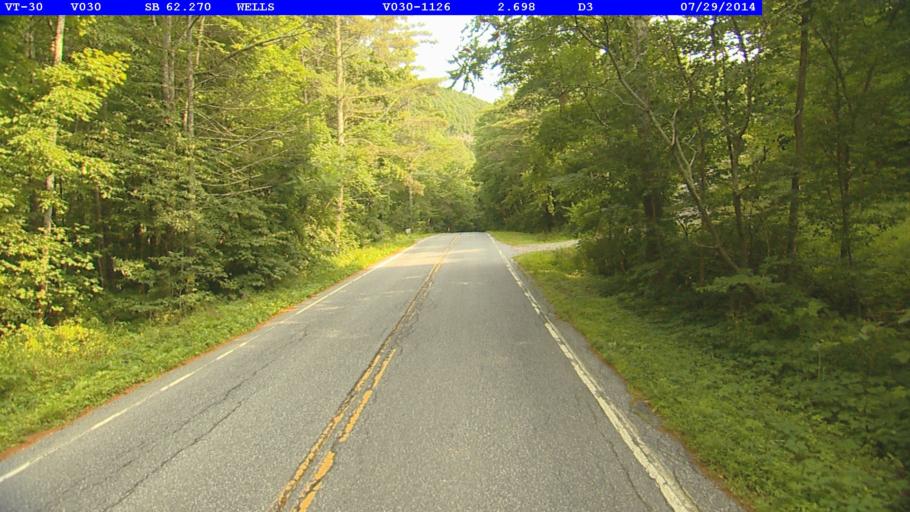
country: US
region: New York
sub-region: Washington County
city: Granville
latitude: 43.4329
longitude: -73.1953
